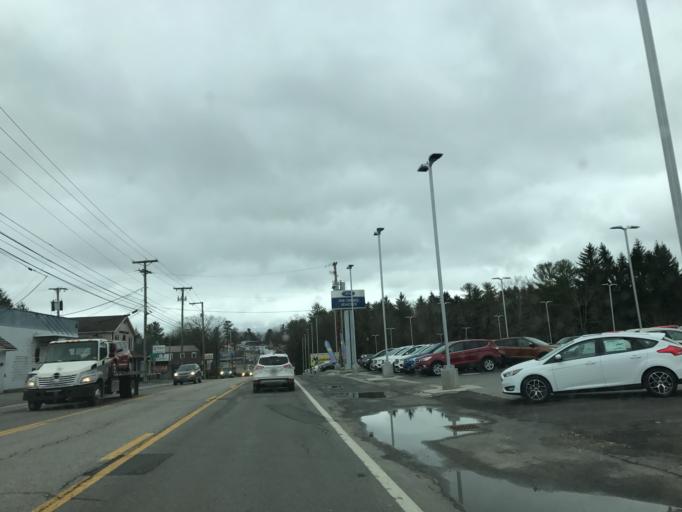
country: US
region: West Virginia
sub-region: Raleigh County
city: Beckley
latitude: 37.7922
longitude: -81.1726
